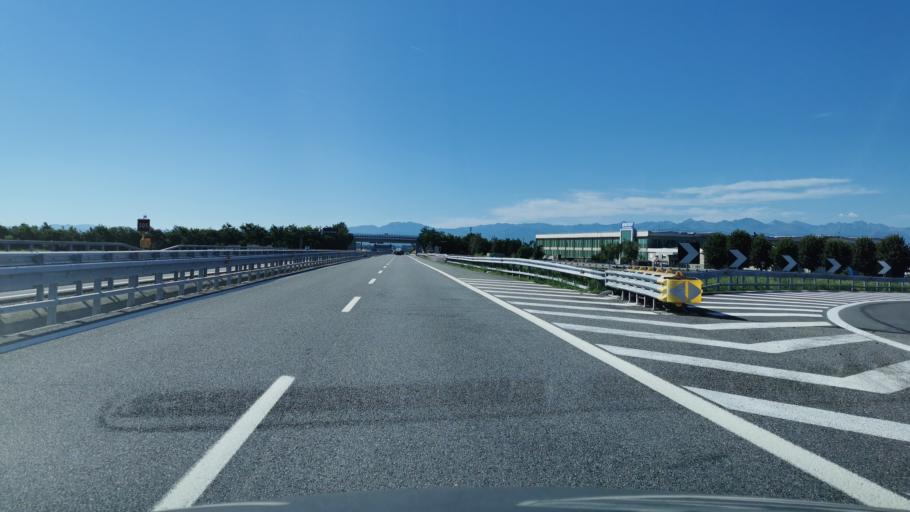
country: IT
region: Piedmont
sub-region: Provincia di Cuneo
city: Bene Vagienna
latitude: 44.5364
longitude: 7.7891
